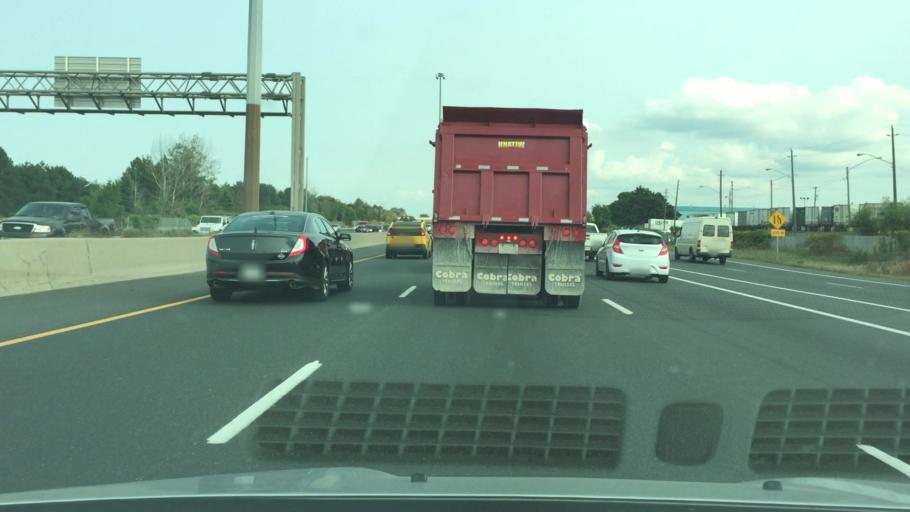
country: CA
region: Ontario
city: Hamilton
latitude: 43.2433
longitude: -79.7439
